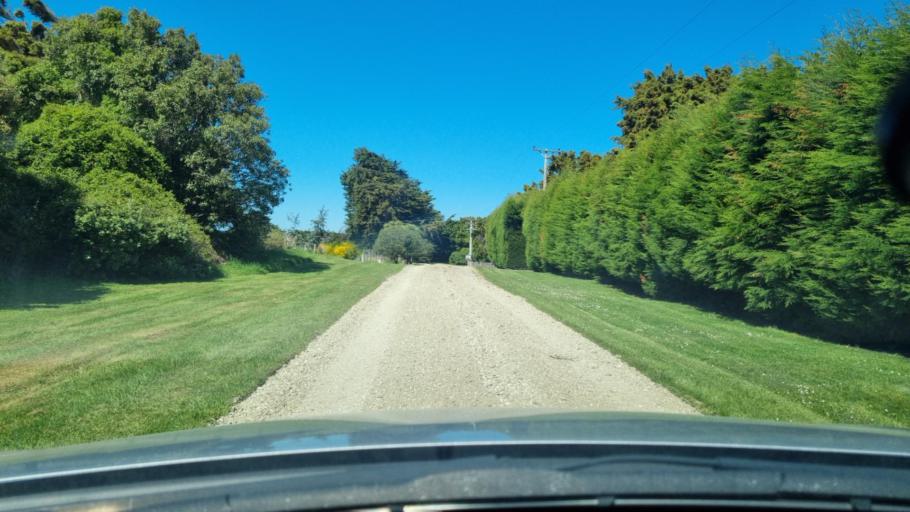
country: NZ
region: Southland
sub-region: Invercargill City
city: Invercargill
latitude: -46.4561
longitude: 168.2813
